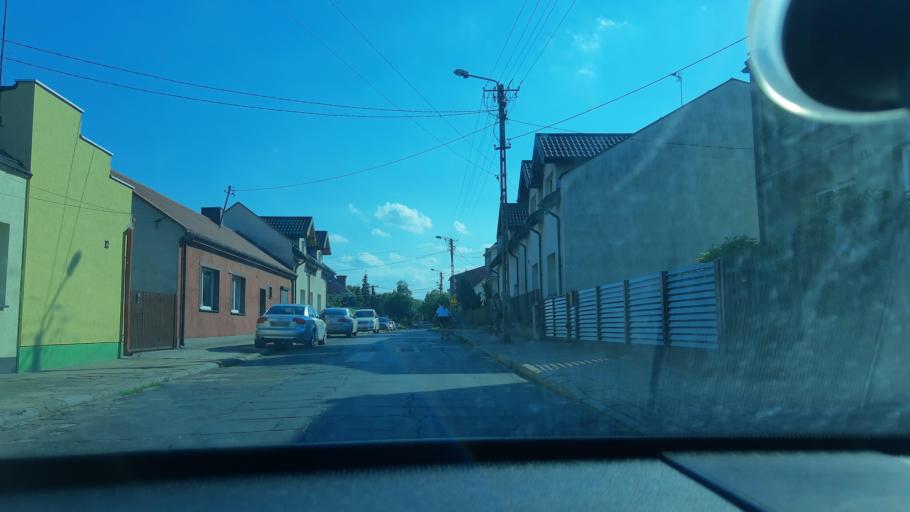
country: PL
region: Lodz Voivodeship
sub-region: Powiat sieradzki
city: Sieradz
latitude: 51.6017
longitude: 18.7321
